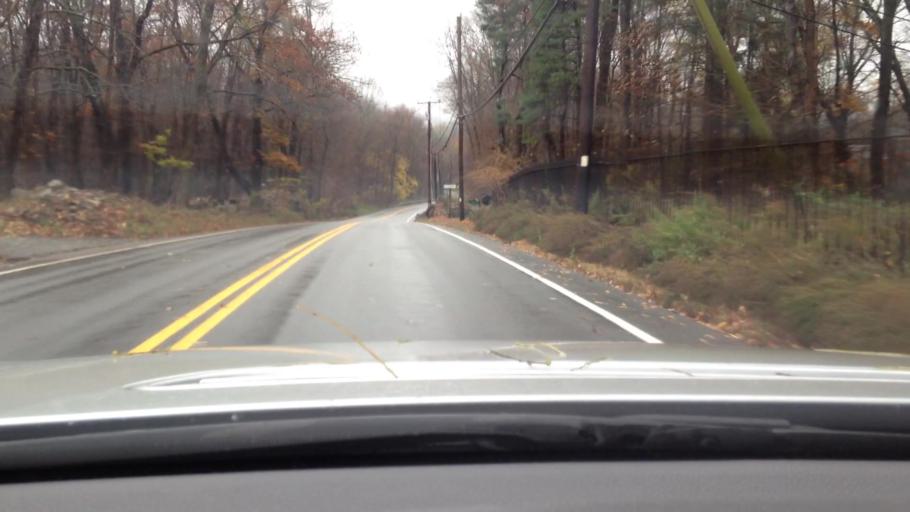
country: US
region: New York
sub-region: Orange County
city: West Point
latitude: 41.3929
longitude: -73.9340
